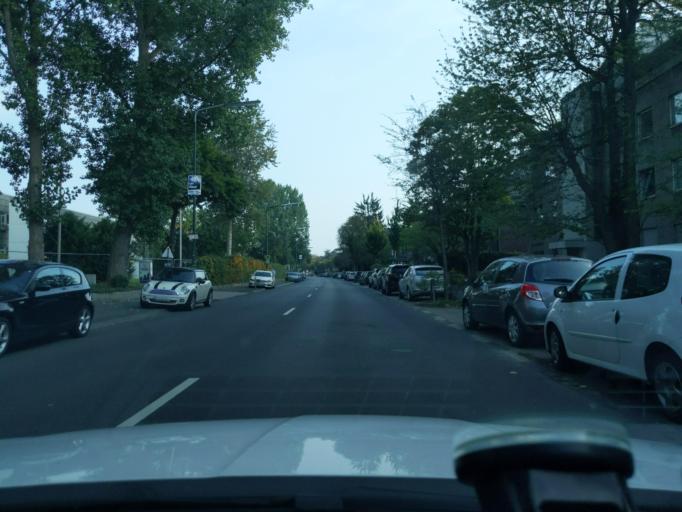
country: DE
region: North Rhine-Westphalia
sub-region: Regierungsbezirk Dusseldorf
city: Dusseldorf
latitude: 51.2374
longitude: 6.8136
